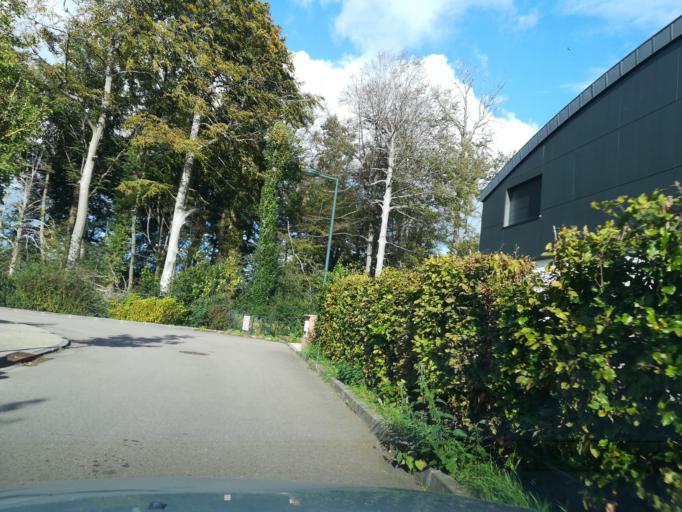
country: FR
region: Haute-Normandie
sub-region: Departement de la Seine-Maritime
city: Bois-Guillaume
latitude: 49.4757
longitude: 1.1300
